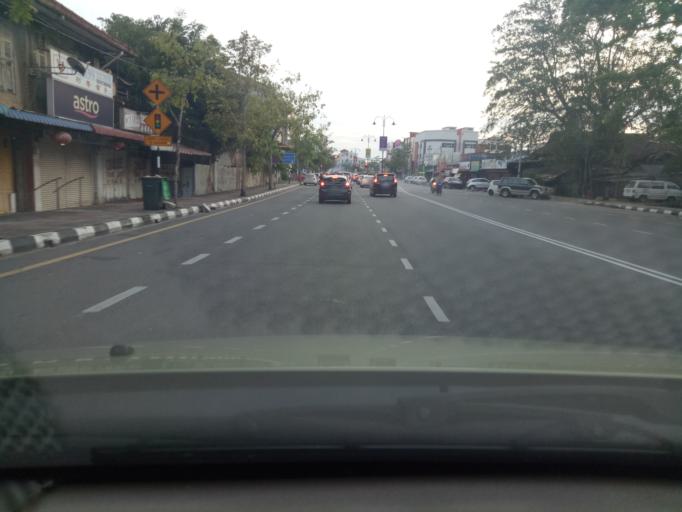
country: MY
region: Kedah
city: Alor Setar
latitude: 6.1151
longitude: 100.3632
